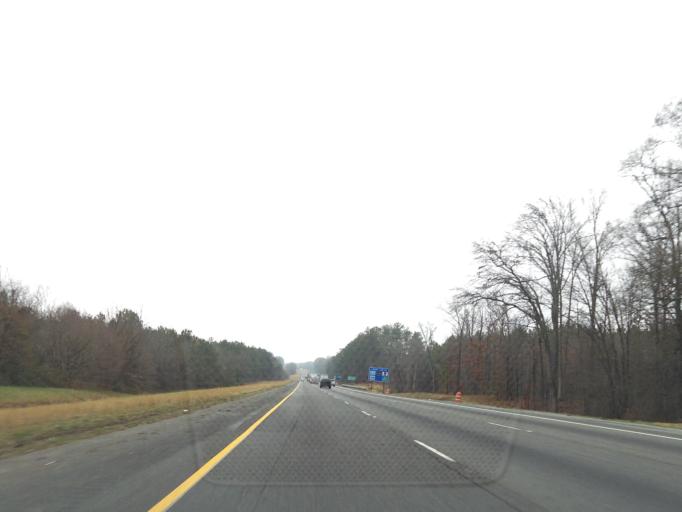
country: US
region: Georgia
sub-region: Henry County
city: McDonough
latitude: 33.3938
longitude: -84.1468
